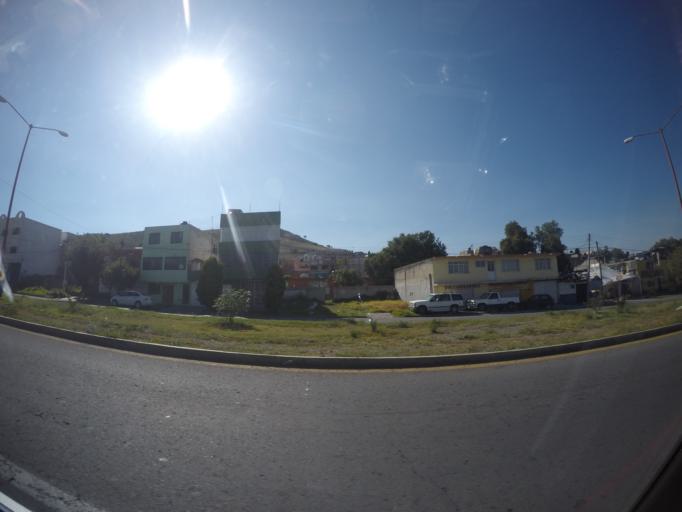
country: MX
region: Hidalgo
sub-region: Mineral de la Reforma
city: Rio de la Soledad
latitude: 20.1163
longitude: -98.7131
